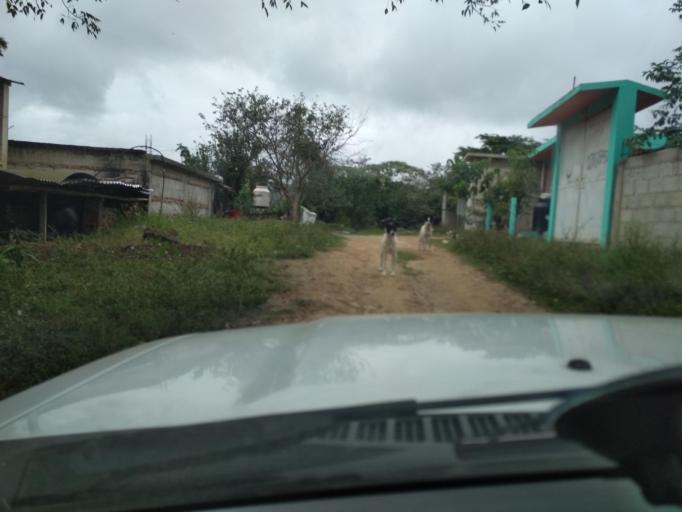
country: MX
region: Veracruz
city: El Castillo
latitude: 19.5473
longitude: -96.8507
